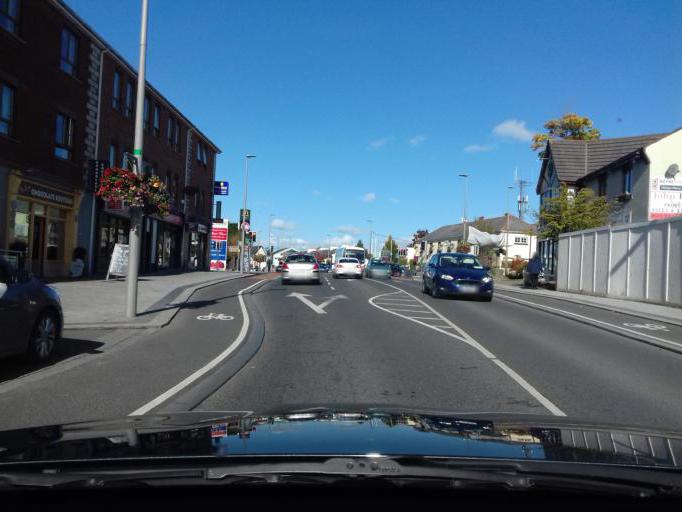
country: IE
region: Leinster
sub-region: An Mhi
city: Ashbourne
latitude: 53.5100
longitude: -6.3965
